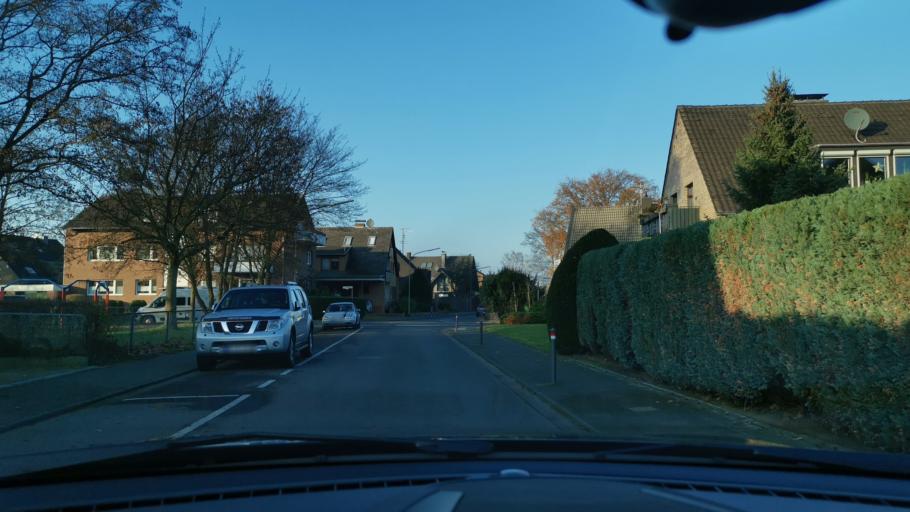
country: DE
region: North Rhine-Westphalia
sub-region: Regierungsbezirk Dusseldorf
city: Neuss
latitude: 51.1450
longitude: 6.7047
